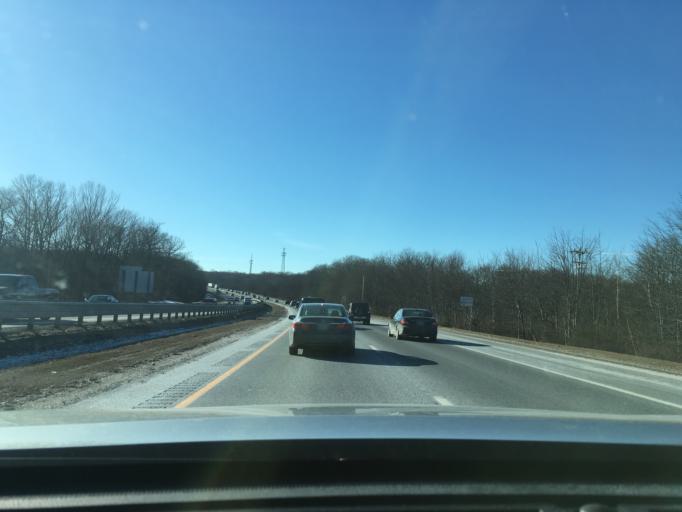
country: US
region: Rhode Island
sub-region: Kent County
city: West Warwick
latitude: 41.6664
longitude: -71.5091
